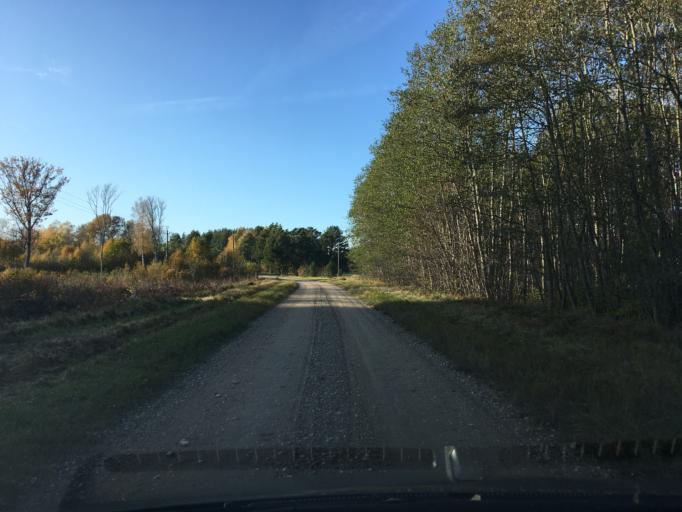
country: EE
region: Laeaene
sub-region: Lihula vald
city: Lihula
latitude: 58.5669
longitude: 23.7644
